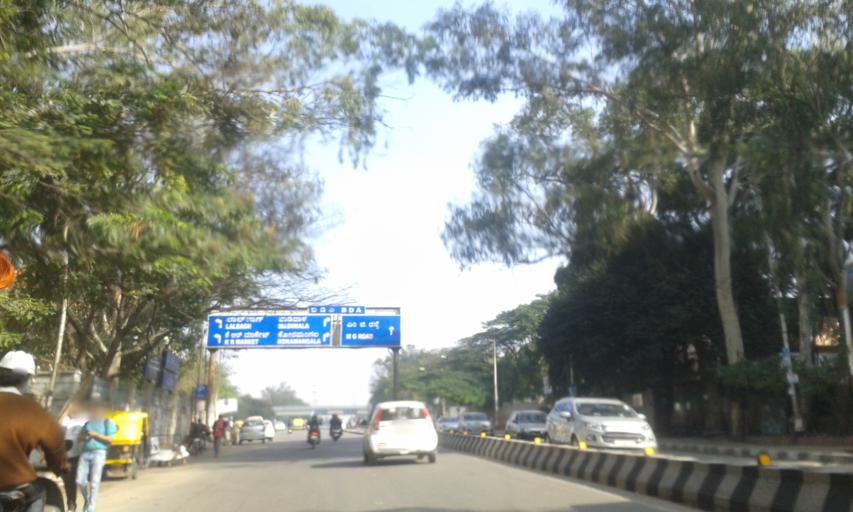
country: IN
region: Karnataka
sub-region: Bangalore Urban
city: Bangalore
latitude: 12.9342
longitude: 77.6012
